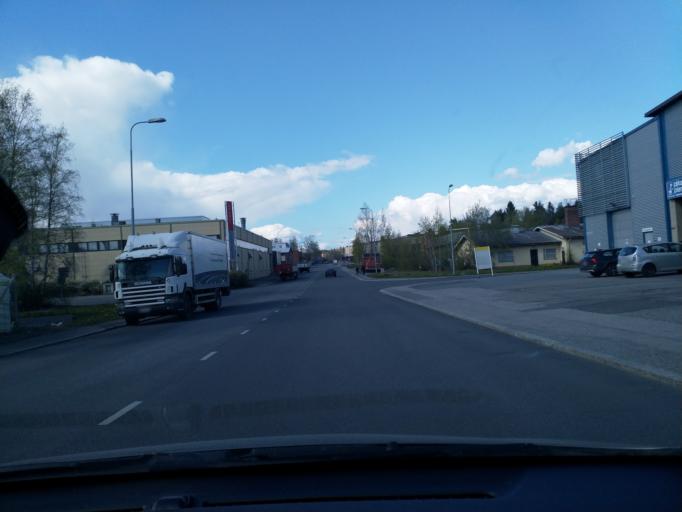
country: FI
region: Pirkanmaa
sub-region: Tampere
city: Tampere
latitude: 61.4792
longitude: 23.7897
